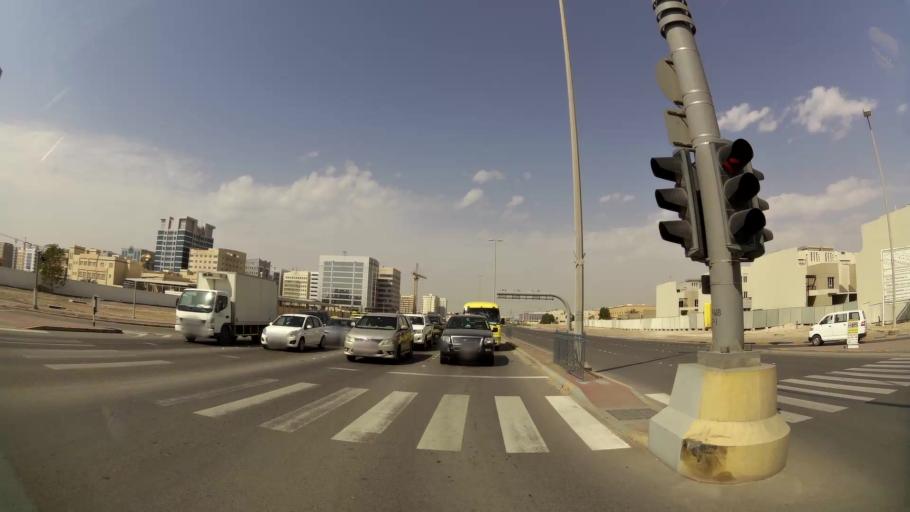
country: AE
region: Abu Dhabi
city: Abu Dhabi
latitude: 24.3381
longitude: 54.5386
